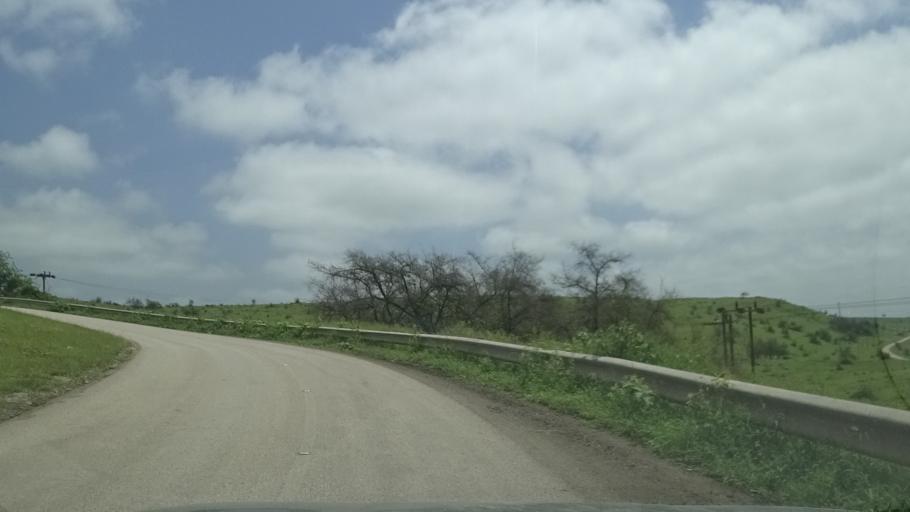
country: OM
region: Zufar
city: Salalah
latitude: 17.2043
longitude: 54.1896
